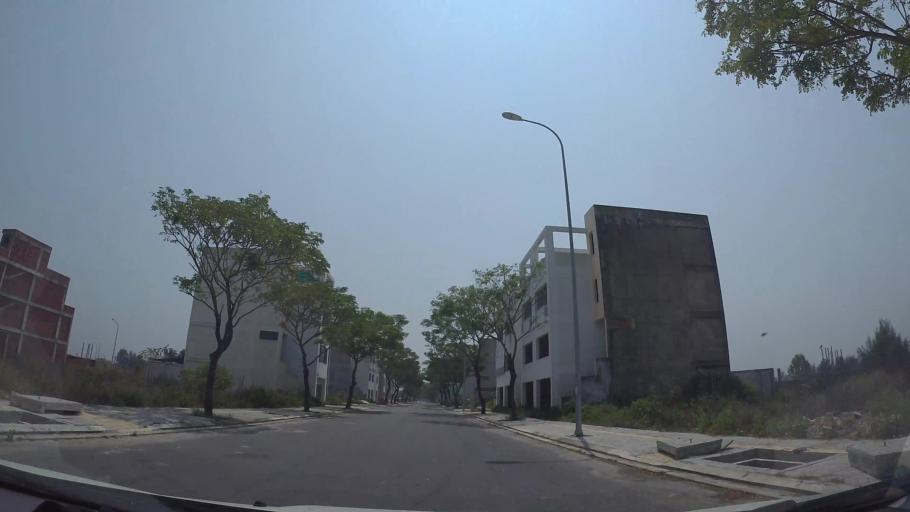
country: VN
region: Da Nang
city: Ngu Hanh Son
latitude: 15.9725
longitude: 108.2609
